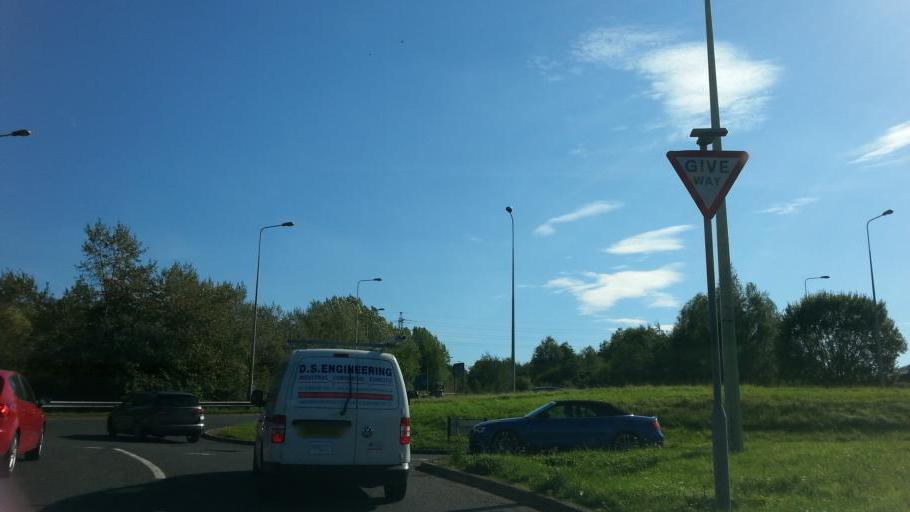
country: GB
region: England
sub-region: Shropshire
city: Hadley
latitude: 52.6932
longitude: -2.4903
